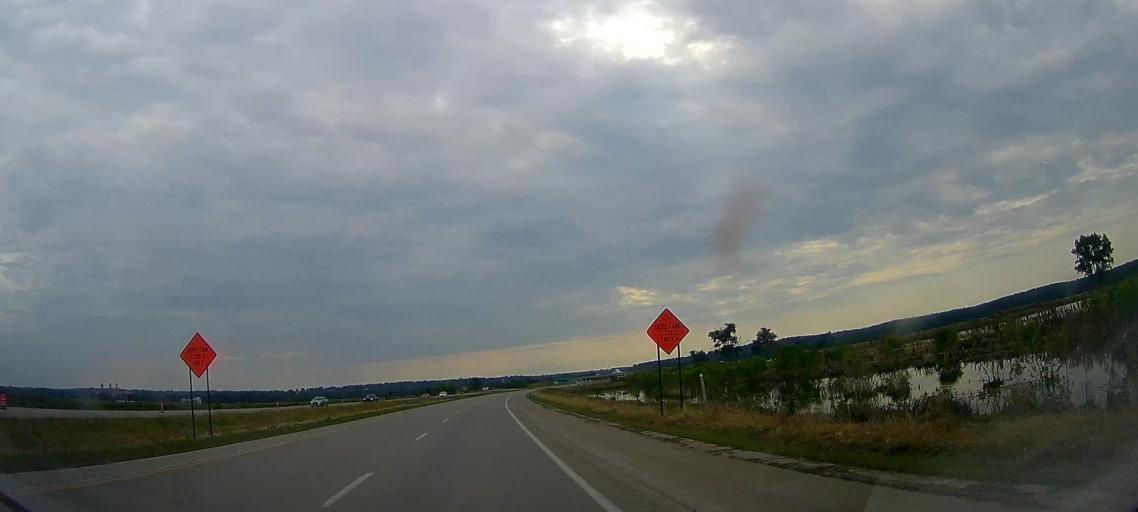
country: US
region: Iowa
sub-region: Pottawattamie County
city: Carter Lake
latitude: 41.3472
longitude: -95.9257
